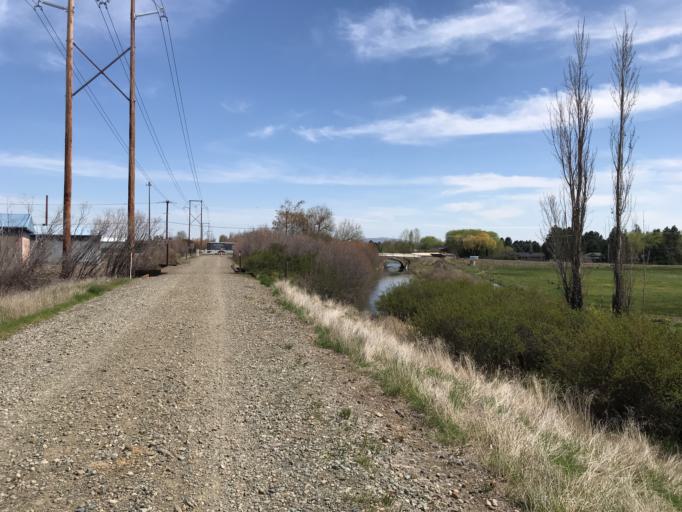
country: US
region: Washington
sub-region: Kittitas County
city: Ellensburg
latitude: 46.9989
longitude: -120.5200
